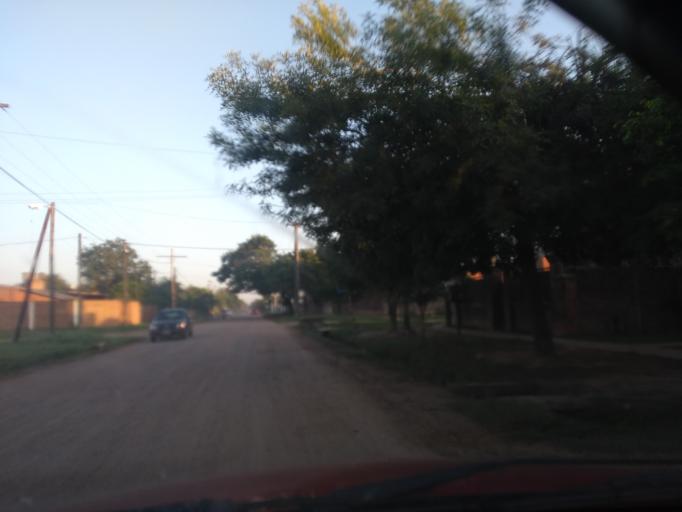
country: AR
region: Chaco
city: Resistencia
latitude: -27.4521
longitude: -58.9642
